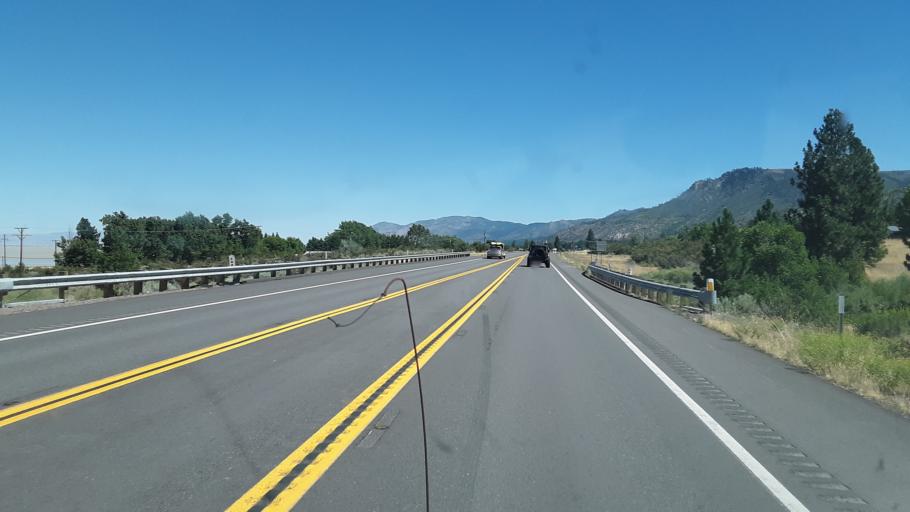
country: US
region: California
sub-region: Lassen County
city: Janesville
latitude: 40.2643
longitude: -120.4727
